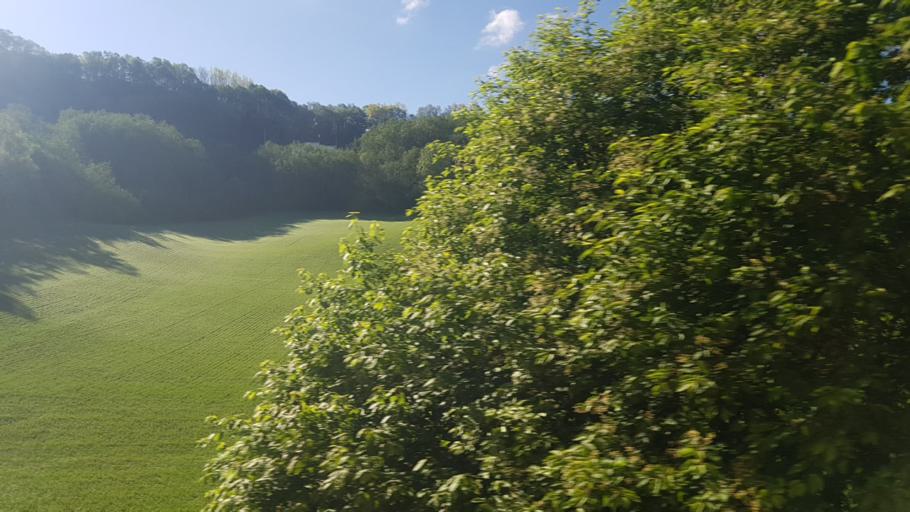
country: NO
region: Sor-Trondelag
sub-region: Melhus
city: Melhus
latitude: 63.3187
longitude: 10.3147
